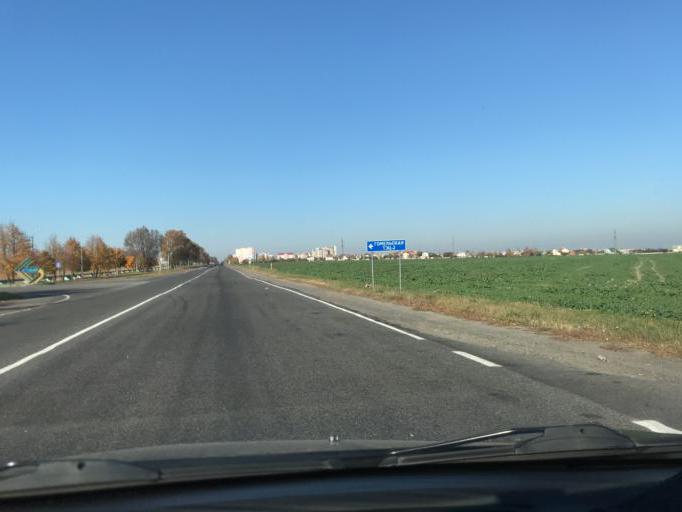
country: BY
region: Gomel
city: Kastsyukowka
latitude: 52.4553
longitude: 30.8212
